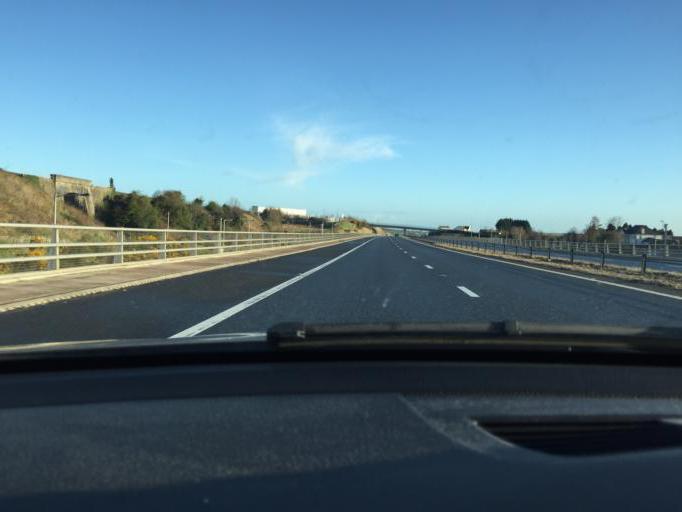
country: GB
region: Northern Ireland
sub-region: Newry and Mourne District
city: Newry
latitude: 54.1845
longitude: -6.3608
